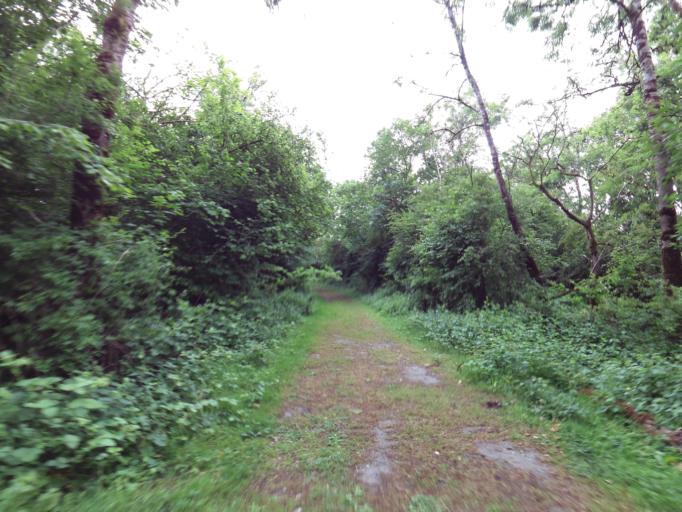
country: IE
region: Connaught
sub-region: County Galway
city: Gort
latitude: 53.0859
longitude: -8.8682
